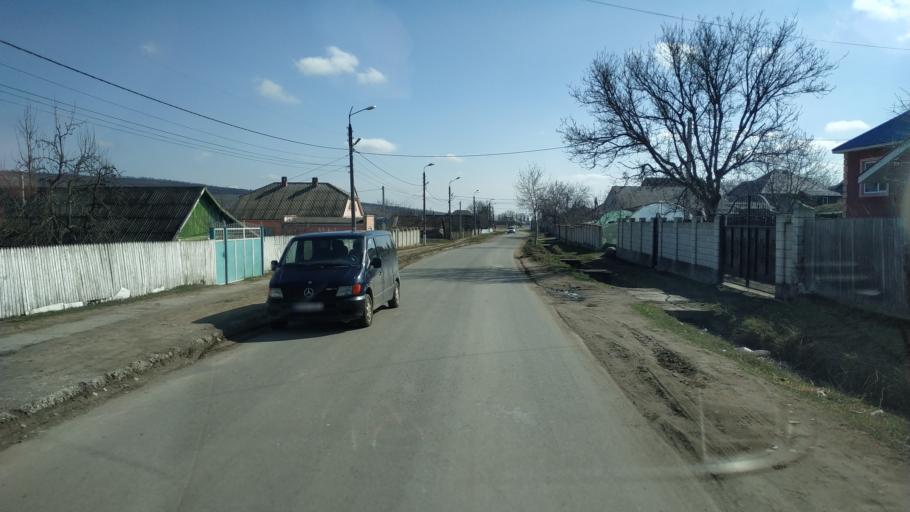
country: MD
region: Hincesti
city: Hincesti
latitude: 46.9660
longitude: 28.5972
